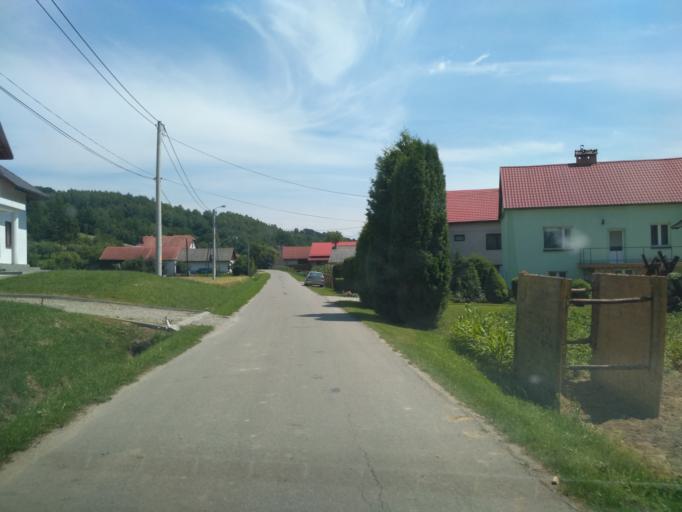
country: PL
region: Subcarpathian Voivodeship
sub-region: Powiat strzyzowski
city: Strzyzow
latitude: 49.8503
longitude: 21.8103
